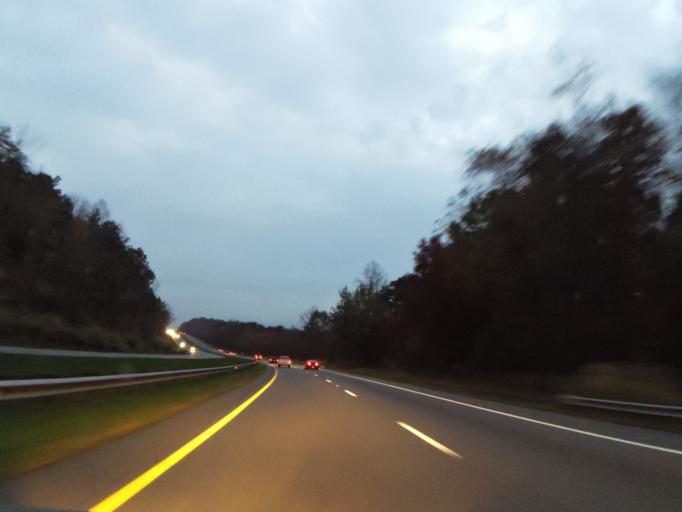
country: US
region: North Carolina
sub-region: McDowell County
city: West Marion
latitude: 35.6352
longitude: -82.0884
